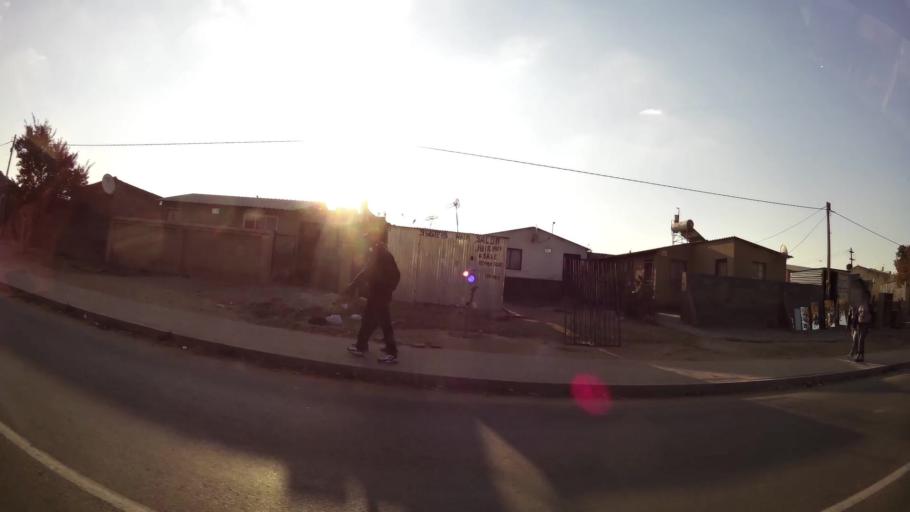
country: ZA
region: Gauteng
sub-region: Ekurhuleni Metropolitan Municipality
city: Tembisa
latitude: -26.0153
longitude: 28.1840
